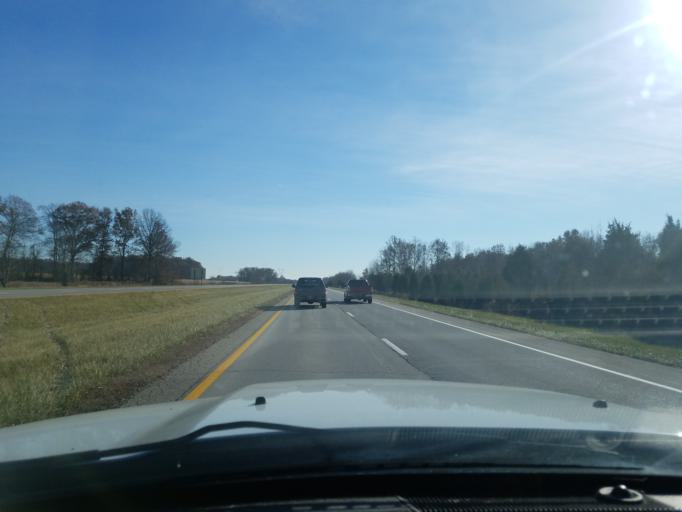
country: US
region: Ohio
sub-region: Brown County
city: Mount Orab
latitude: 39.0361
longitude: -83.9041
